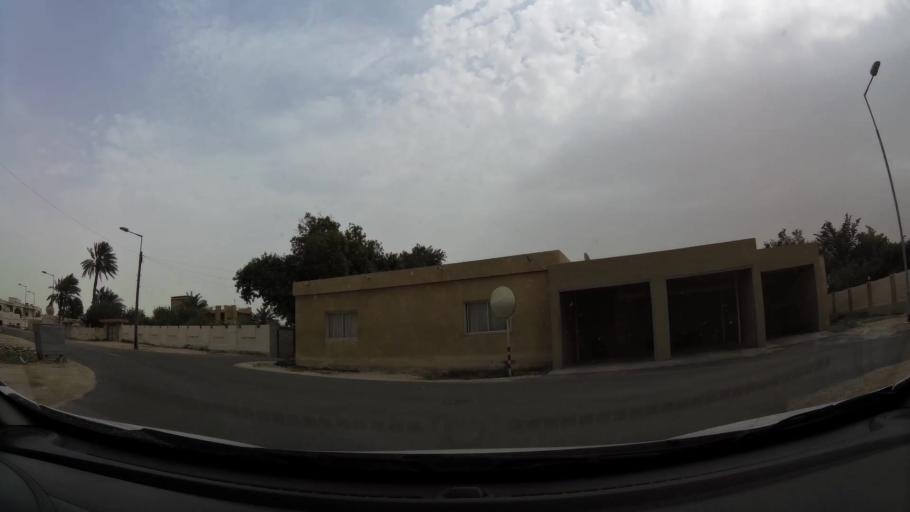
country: BH
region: Central Governorate
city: Madinat Hamad
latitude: 26.1175
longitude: 50.5294
